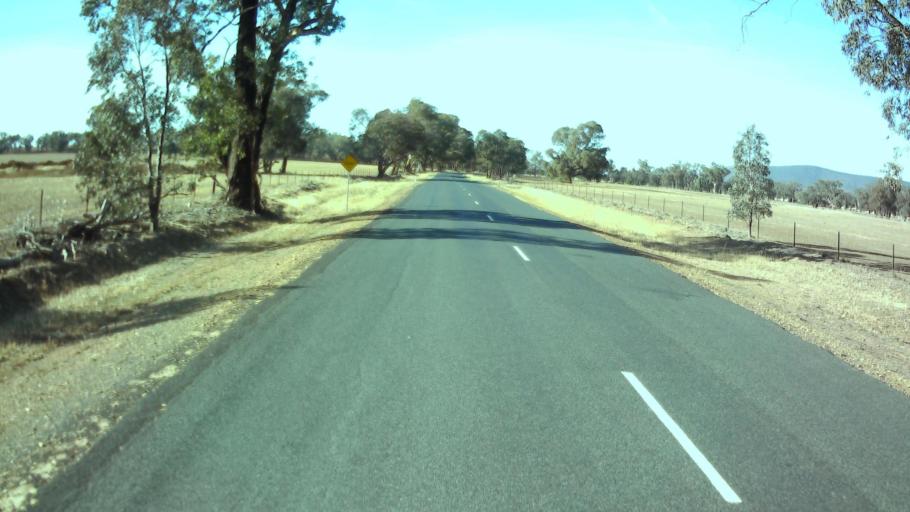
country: AU
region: New South Wales
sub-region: Weddin
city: Grenfell
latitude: -33.9363
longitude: 148.1376
